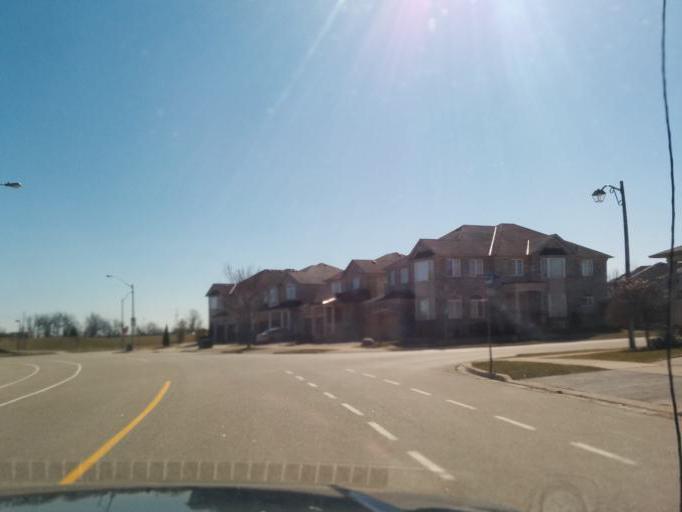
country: CA
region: Ontario
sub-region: Halton
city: Milton
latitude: 43.5066
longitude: -79.8423
